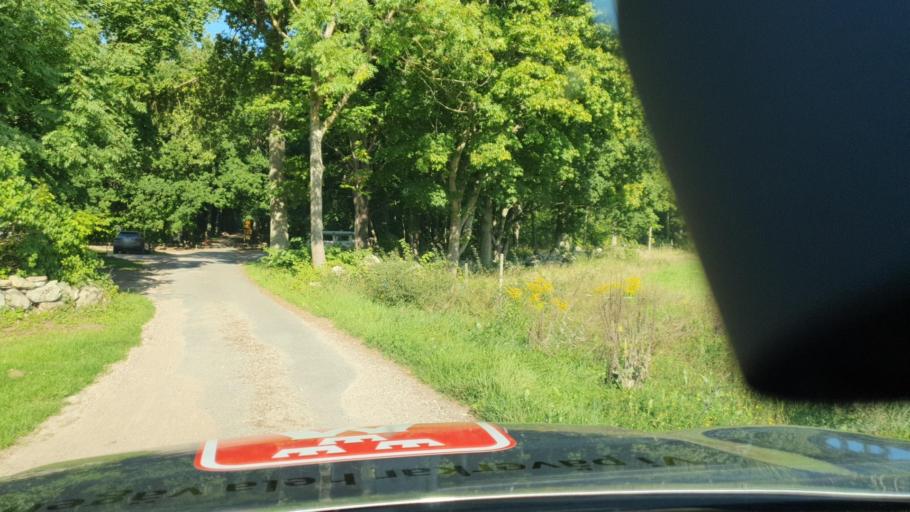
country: SE
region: Skane
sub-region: Kristianstads Kommun
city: Fjalkinge
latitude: 56.0731
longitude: 14.3590
